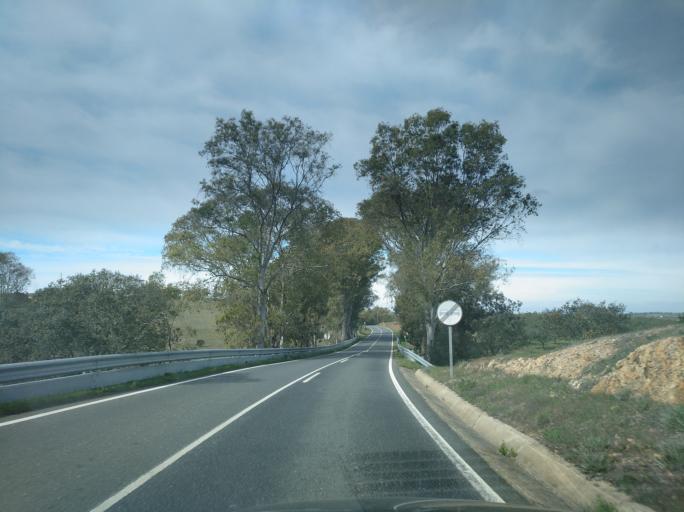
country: PT
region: Beja
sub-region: Mertola
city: Mertola
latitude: 37.7192
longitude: -7.7594
